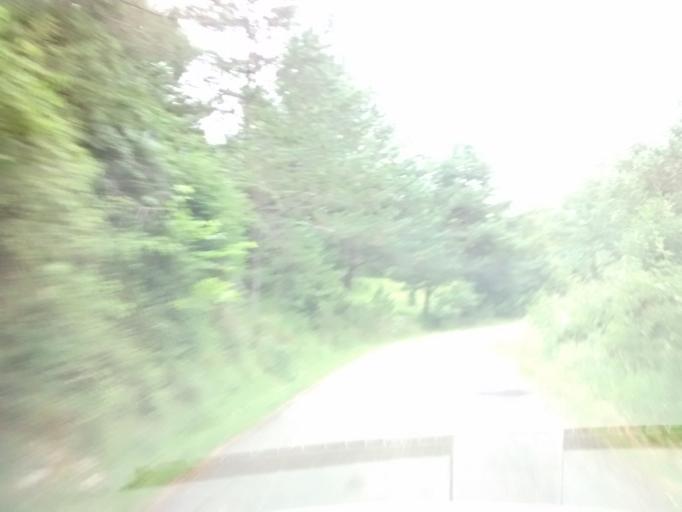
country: ES
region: Aragon
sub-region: Provincia de Huesca
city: Puertolas
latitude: 42.5834
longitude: 0.1427
